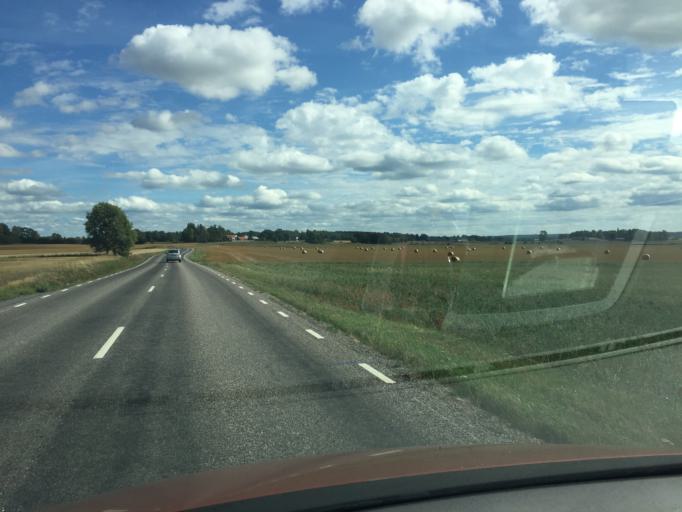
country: SE
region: OErebro
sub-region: Hallsbergs Kommun
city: Hallsberg
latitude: 59.1203
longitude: 15.0010
